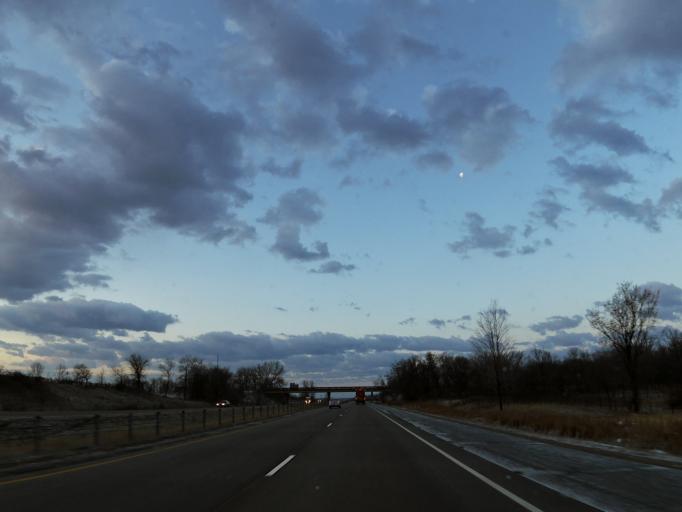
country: US
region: Minnesota
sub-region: Dakota County
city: Lakeville
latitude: 44.6258
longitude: -93.2985
